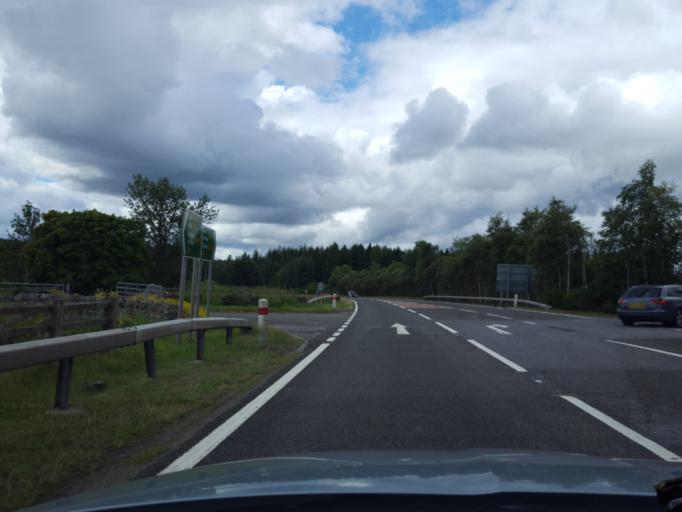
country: GB
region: Scotland
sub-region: Highland
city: Grantown on Spey
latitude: 57.3046
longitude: -3.6546
